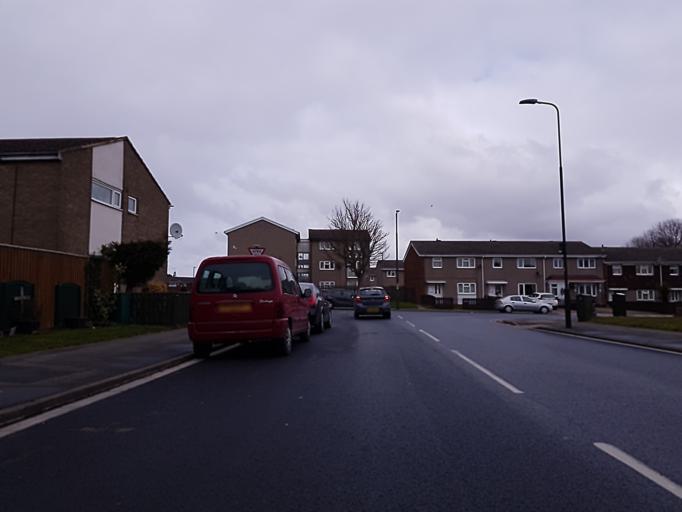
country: GB
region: England
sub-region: North East Lincolnshire
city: Great Coates
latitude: 53.5712
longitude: -0.1255
